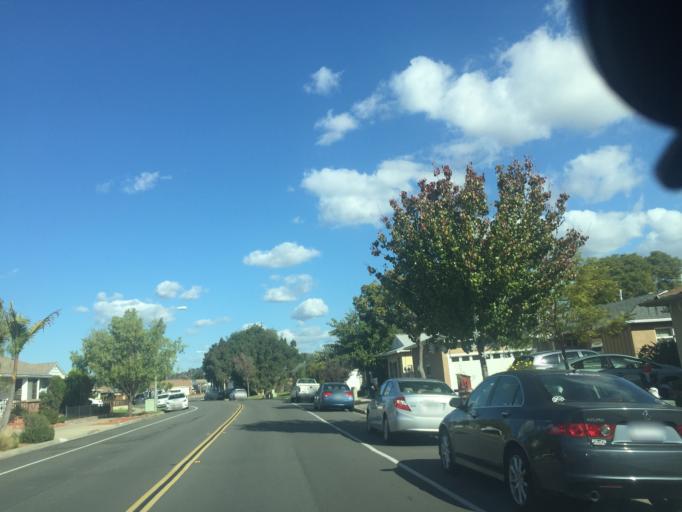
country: US
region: California
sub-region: San Diego County
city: La Mesa
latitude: 32.7897
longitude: -117.0860
